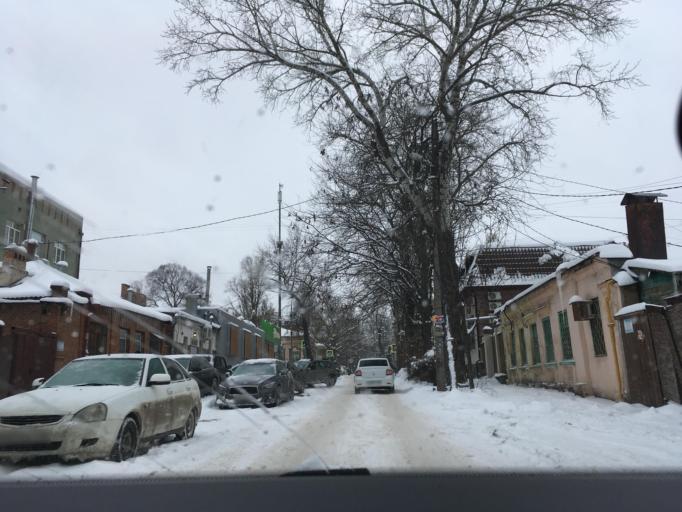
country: RU
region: Rostov
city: Rostov-na-Donu
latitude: 47.2284
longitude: 39.7549
